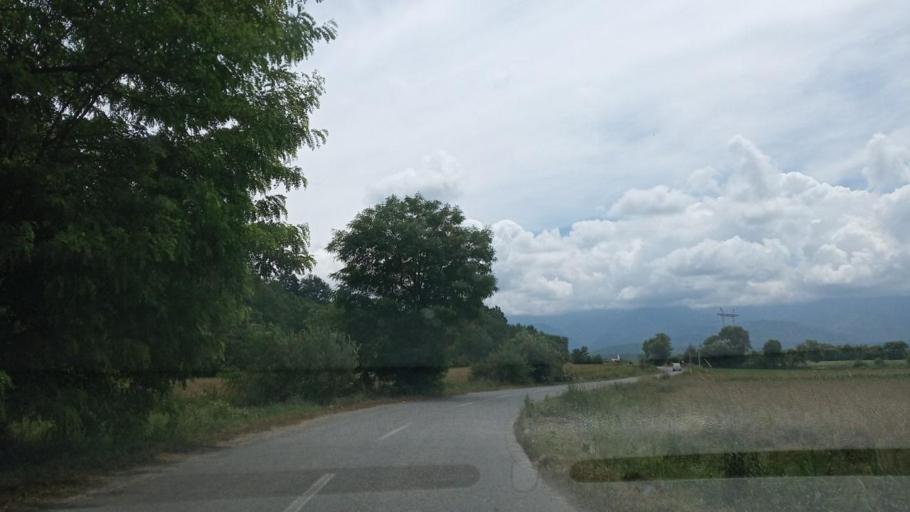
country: RO
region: Sibiu
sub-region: Comuna Porumbacu de Jos
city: Porumbacu de Jos
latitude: 45.7313
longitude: 24.4700
